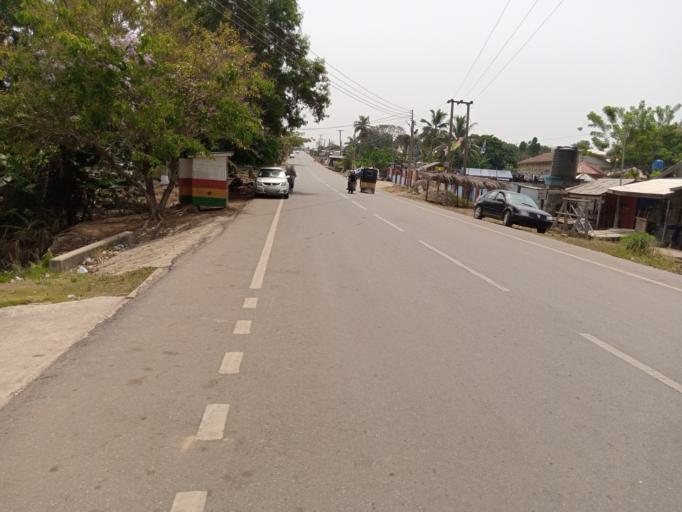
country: GH
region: Volta
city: Kpandu
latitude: 7.0071
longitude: 0.2957
